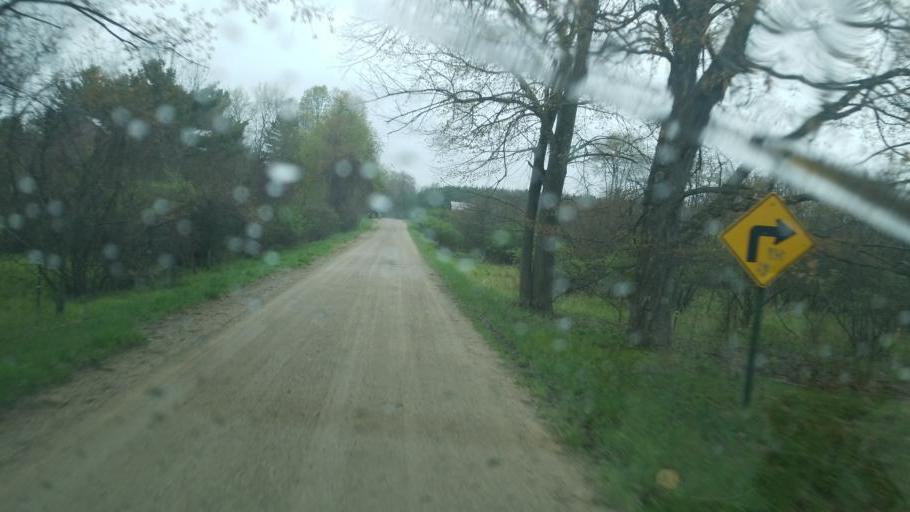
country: US
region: Michigan
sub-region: Mecosta County
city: Canadian Lakes
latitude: 43.5234
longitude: -85.3139
